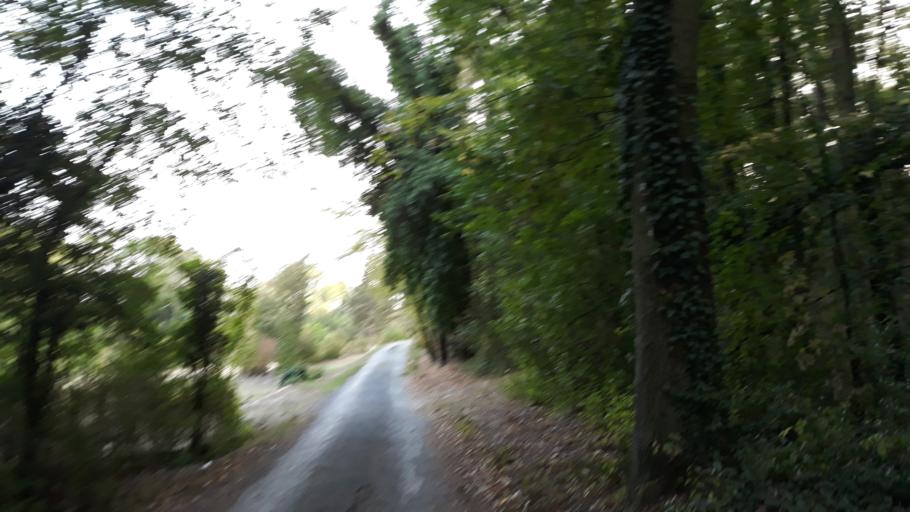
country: FR
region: Picardie
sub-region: Departement de l'Aisne
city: Laon
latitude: 49.5527
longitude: 3.6167
